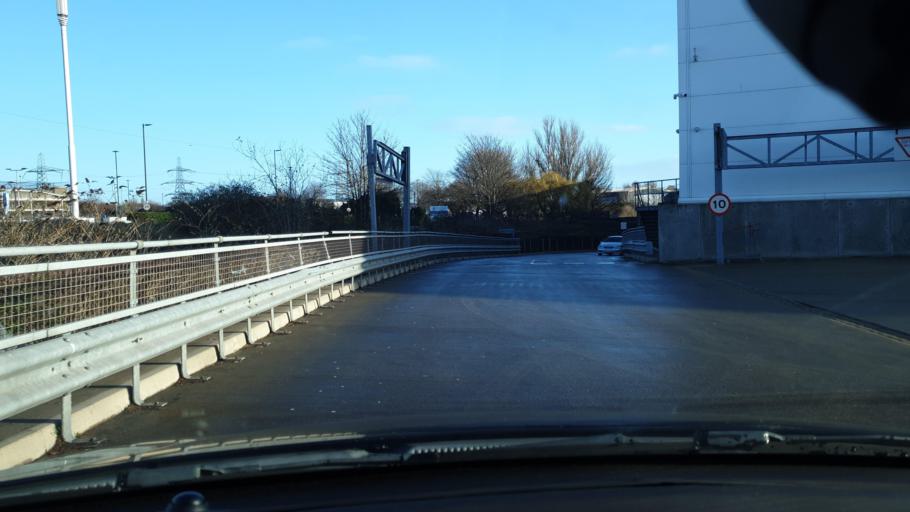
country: GB
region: England
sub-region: City and Borough of Birmingham
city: Birmingham
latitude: 52.5031
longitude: -1.8553
